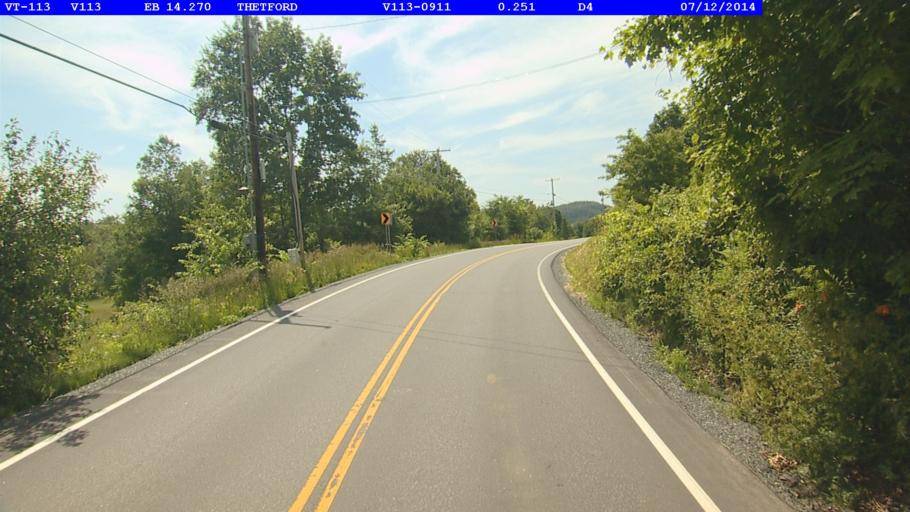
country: US
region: New Hampshire
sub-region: Grafton County
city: Orford
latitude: 43.8940
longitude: -72.2586
